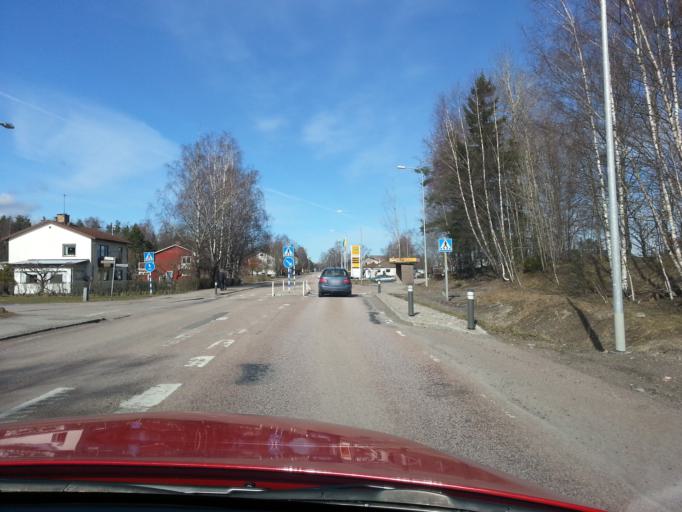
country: SE
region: Uppsala
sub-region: Osthammars Kommun
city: Gimo
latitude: 60.1672
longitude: 18.1937
